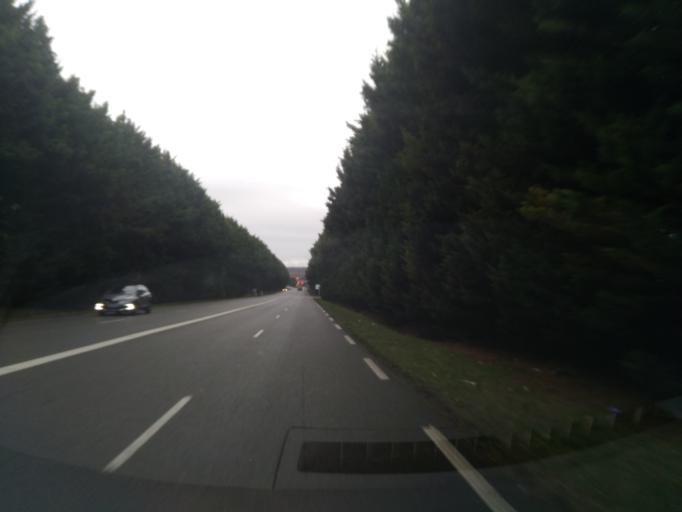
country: FR
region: Ile-de-France
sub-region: Departement des Yvelines
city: Villepreux
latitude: 48.8208
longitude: 2.0102
